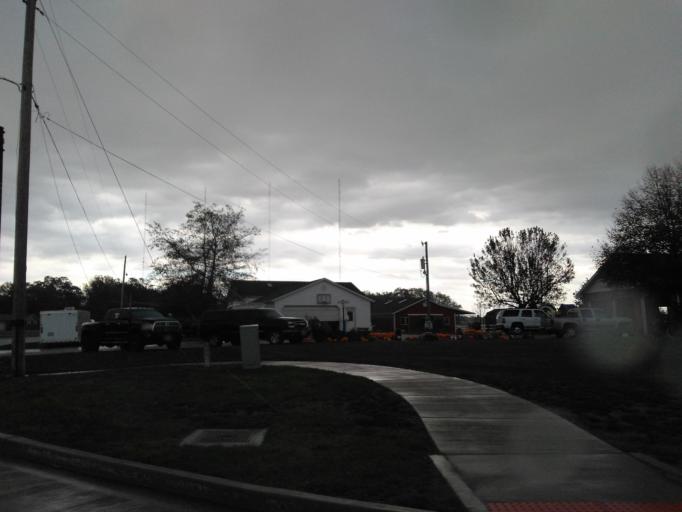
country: US
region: Illinois
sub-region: Madison County
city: Highland
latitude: 38.7571
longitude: -89.6608
